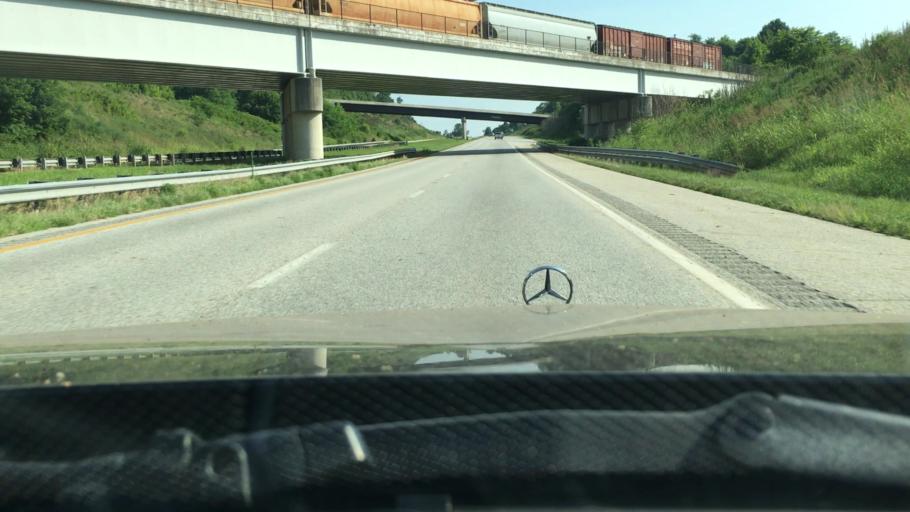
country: US
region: Virginia
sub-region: Amherst County
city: Amherst
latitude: 37.5541
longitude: -79.0663
